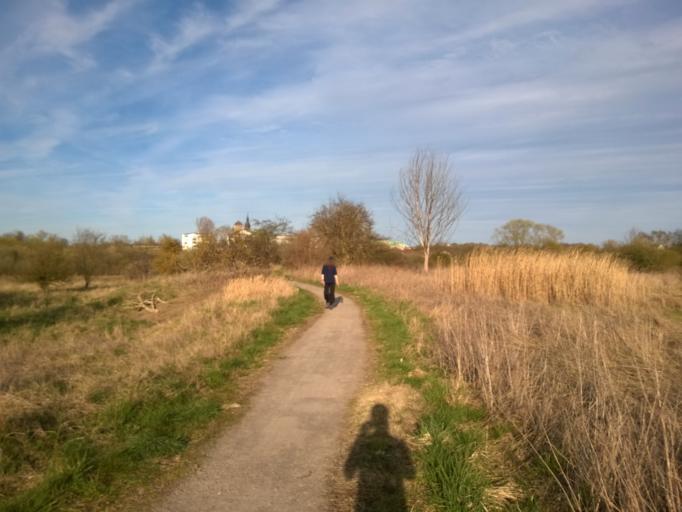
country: SE
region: Skane
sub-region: Kristianstads Kommun
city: Kristianstad
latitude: 56.0301
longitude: 14.1415
